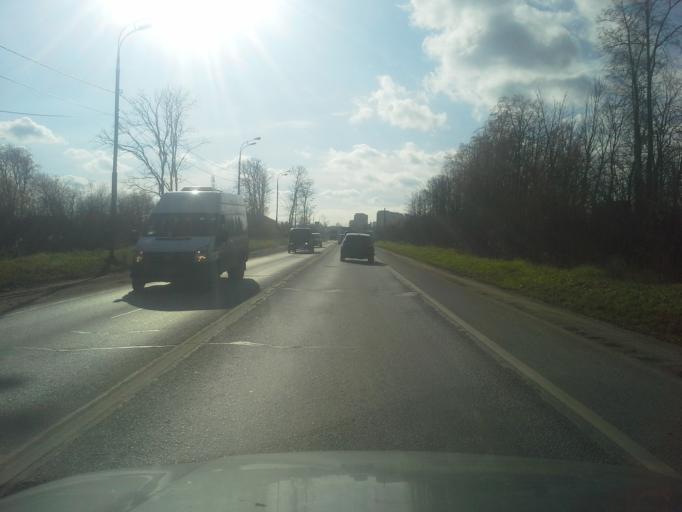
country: RU
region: Moskovskaya
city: Bol'shiye Vyazemy
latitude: 55.6347
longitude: 36.9838
